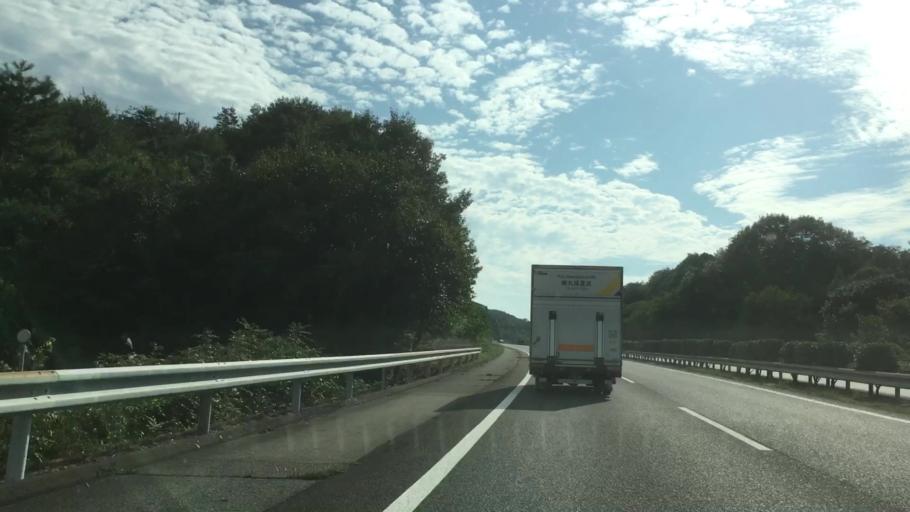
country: JP
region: Yamaguchi
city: Yanai
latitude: 34.0767
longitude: 132.0699
